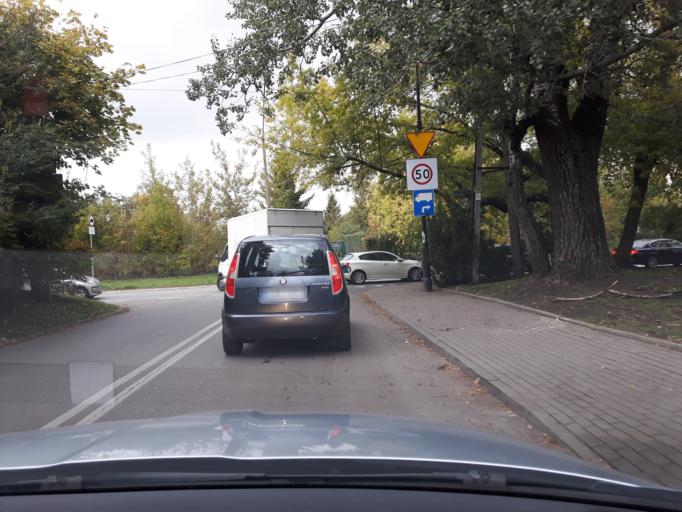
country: PL
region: Masovian Voivodeship
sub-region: Warszawa
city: Mokotow
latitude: 52.1886
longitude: 21.0348
